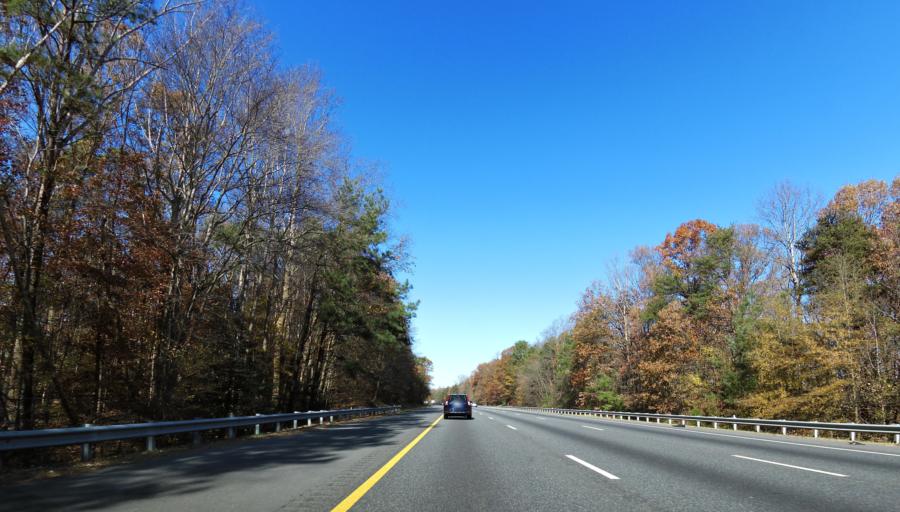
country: US
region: Virginia
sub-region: Caroline County
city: Bowling Green
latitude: 37.9548
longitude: -77.4819
